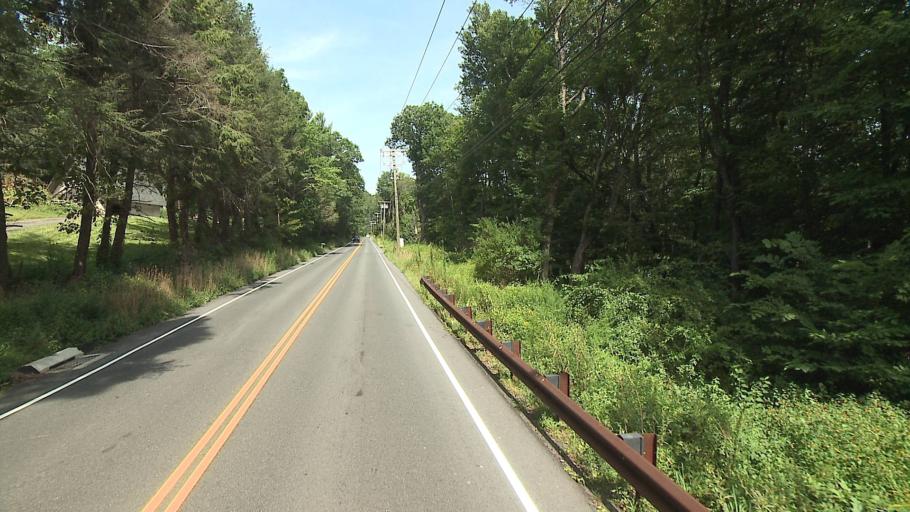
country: US
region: Connecticut
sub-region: Litchfield County
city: Bethlehem Village
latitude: 41.6056
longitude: -73.1760
